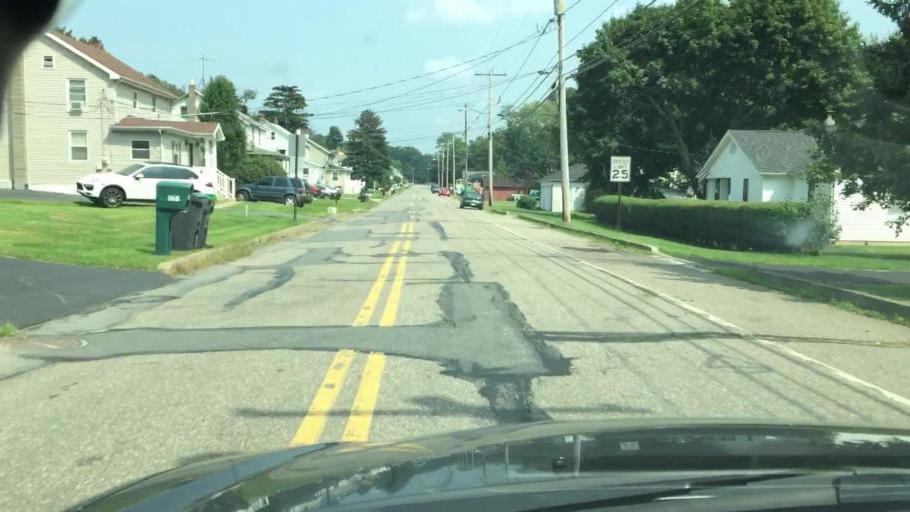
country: US
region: Pennsylvania
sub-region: Luzerne County
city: Harleigh
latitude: 40.9941
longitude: -76.0001
